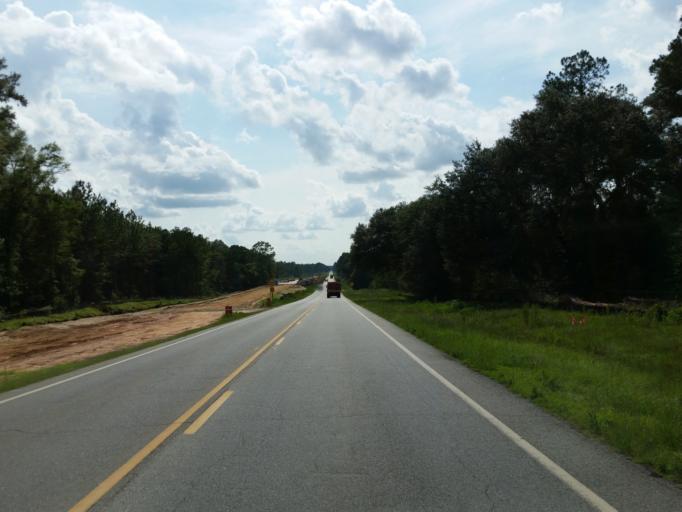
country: US
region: Georgia
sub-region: Lee County
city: Leesburg
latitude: 31.7249
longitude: -84.0135
